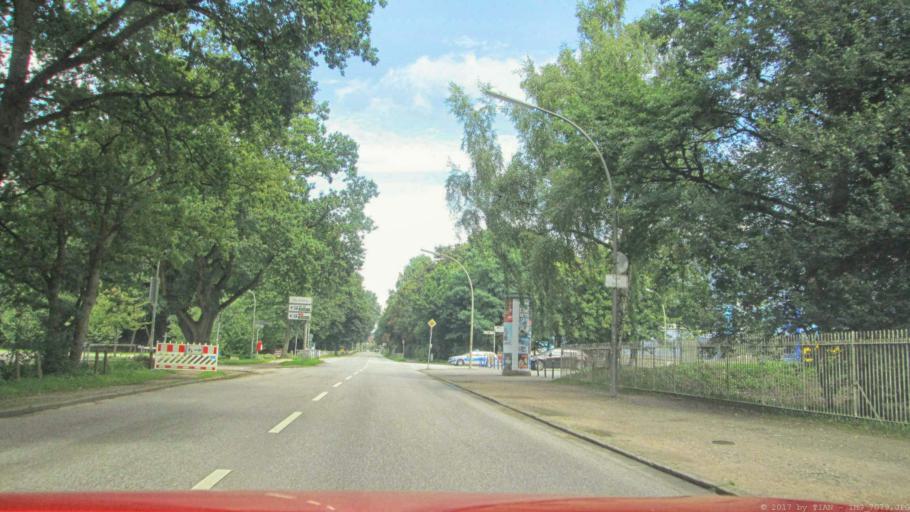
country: DE
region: Hamburg
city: Eidelstedt
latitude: 53.5888
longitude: 9.8971
